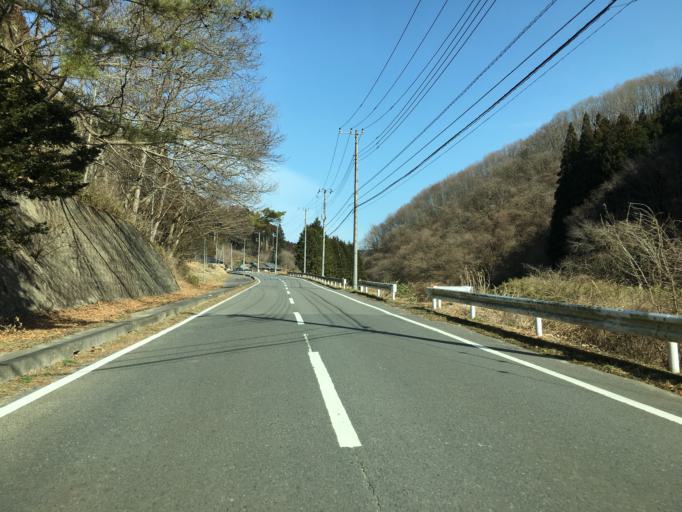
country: JP
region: Ibaraki
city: Daigo
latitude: 36.8215
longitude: 140.5274
